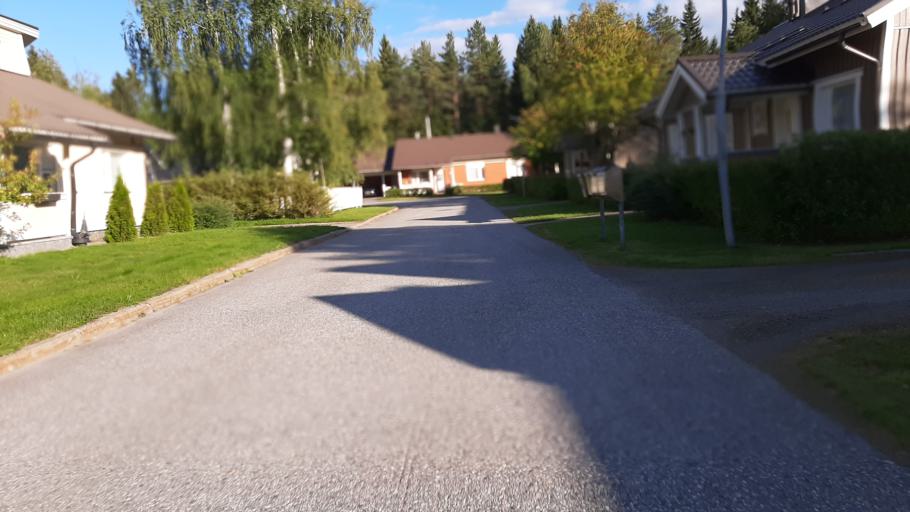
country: FI
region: North Karelia
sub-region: Joensuu
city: Joensuu
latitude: 62.6233
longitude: 29.7978
